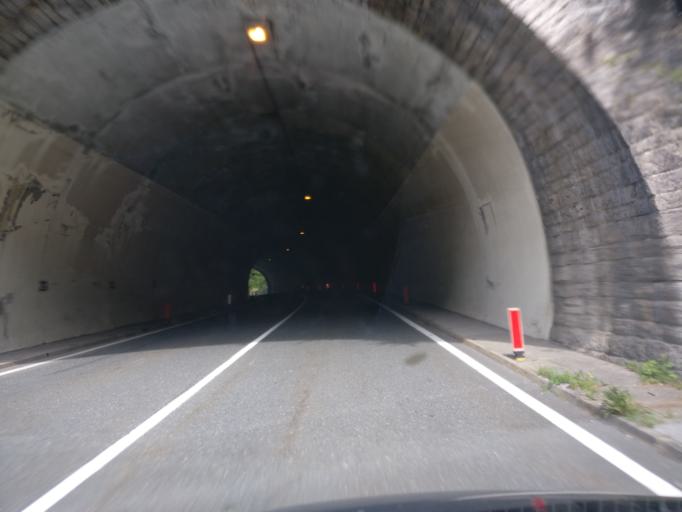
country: AT
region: Salzburg
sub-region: Politischer Bezirk Hallein
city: Scheffau am Tennengebirge
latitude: 47.5757
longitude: 13.1947
